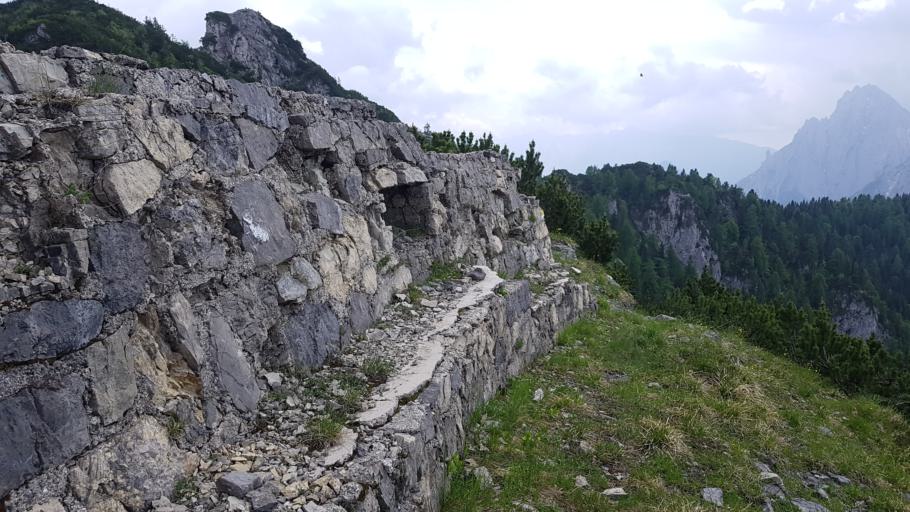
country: IT
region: Friuli Venezia Giulia
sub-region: Provincia di Udine
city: Paularo
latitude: 46.5210
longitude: 13.1791
